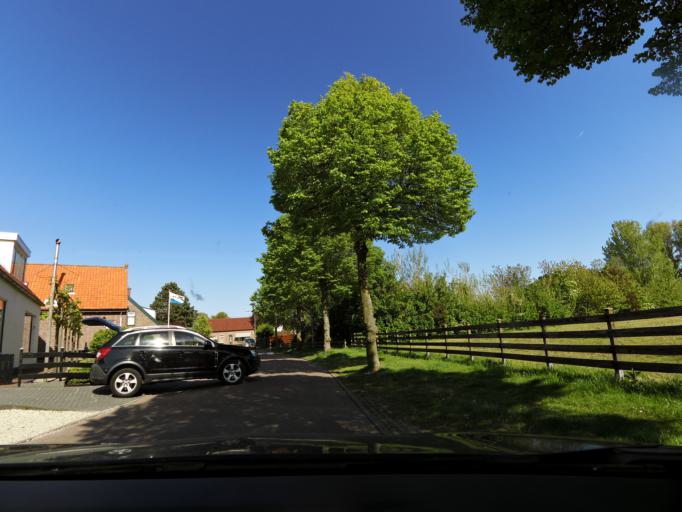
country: NL
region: South Holland
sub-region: Gemeente Goeree-Overflakkee
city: Ouddorp
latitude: 51.8022
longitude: 3.9315
